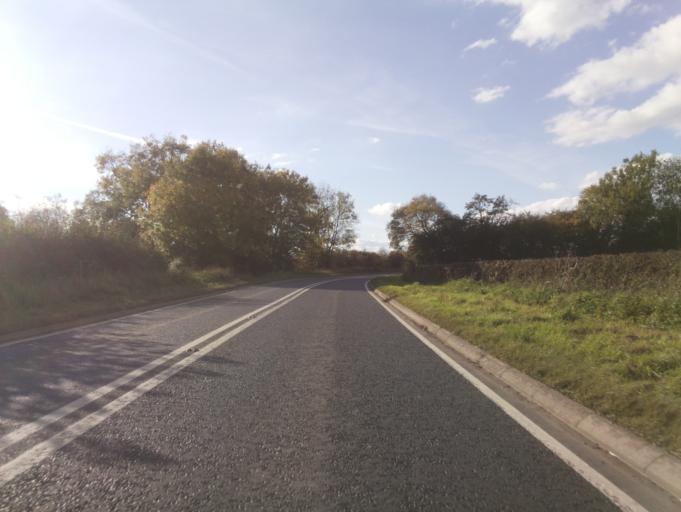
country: GB
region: England
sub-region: Herefordshire
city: Kinnersley
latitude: 52.1184
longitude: -2.9864
